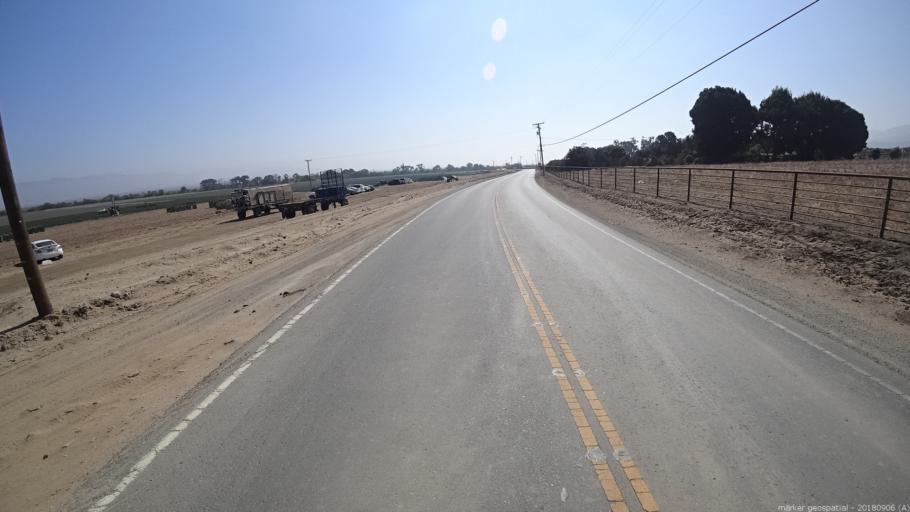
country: US
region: California
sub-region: Monterey County
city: Chualar
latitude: 36.5623
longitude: -121.5588
